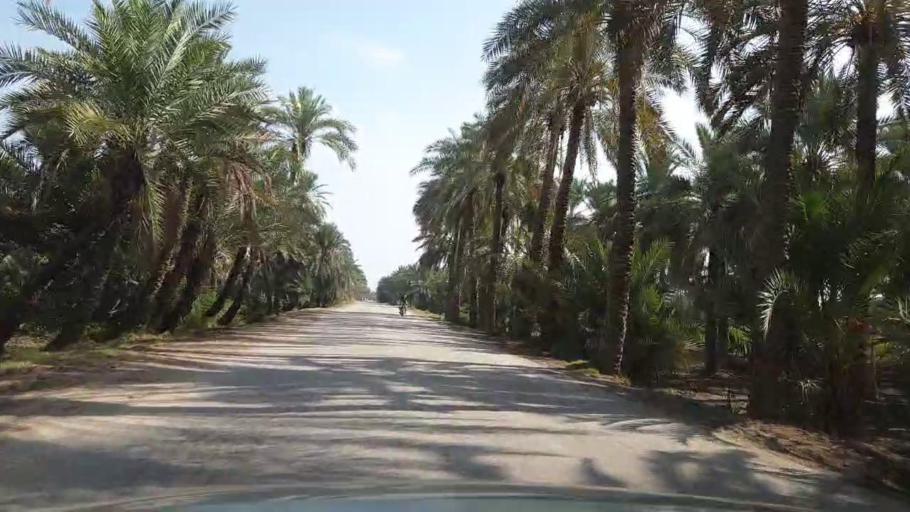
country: PK
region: Sindh
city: Rohri
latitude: 27.6688
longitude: 68.8783
